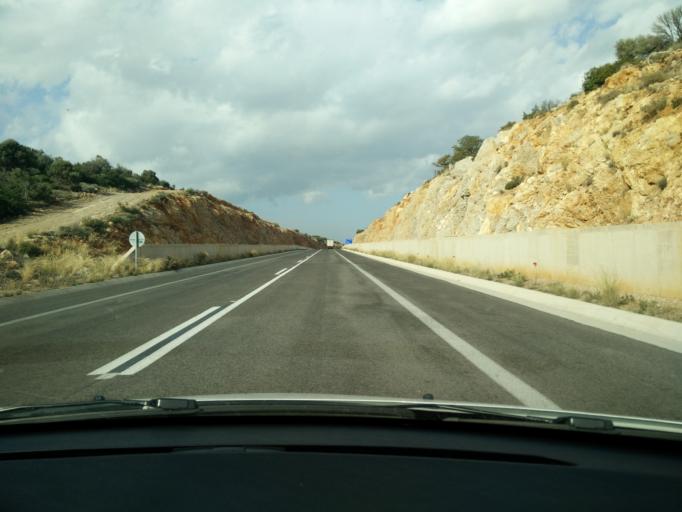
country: GR
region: Crete
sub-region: Nomos Lasithiou
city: Agios Nikolaos
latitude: 35.1702
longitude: 25.7020
